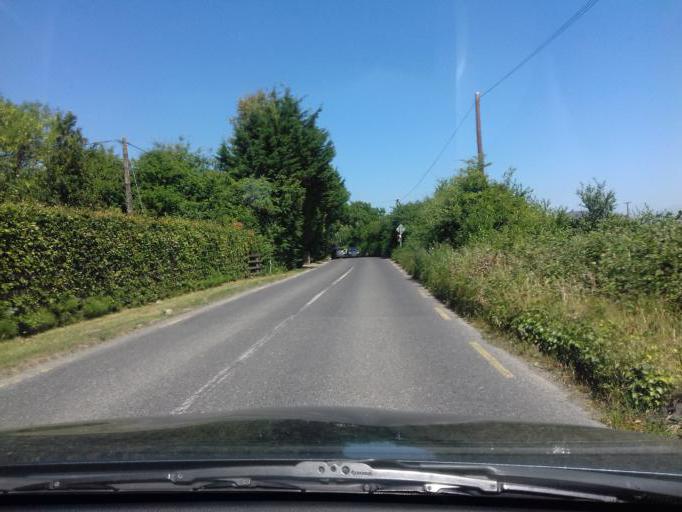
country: IE
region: Leinster
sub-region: Fingal County
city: Swords
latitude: 53.5057
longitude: -6.2676
